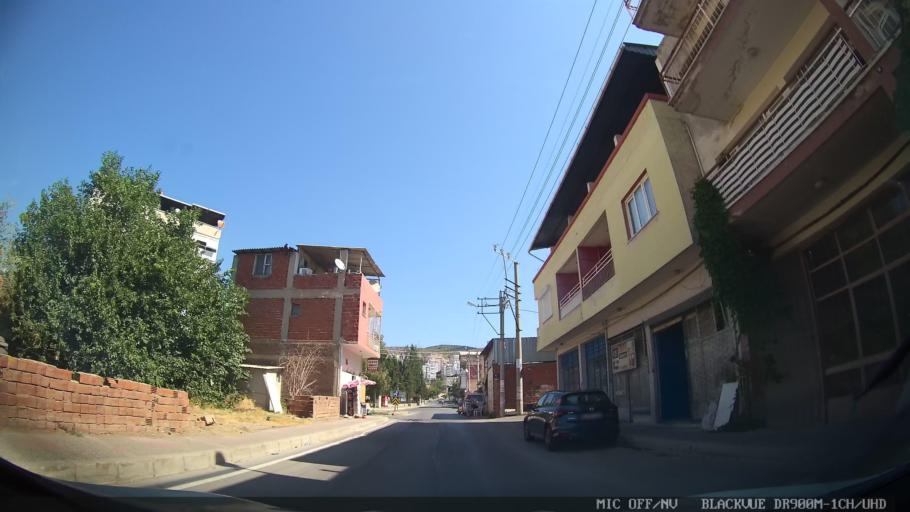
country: TR
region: Izmir
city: Karsiyaka
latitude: 38.4969
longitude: 27.0676
